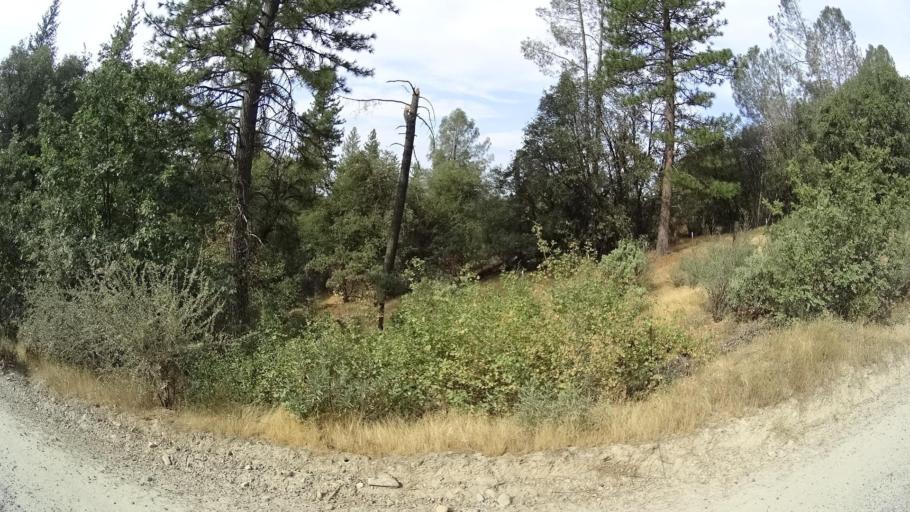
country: US
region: California
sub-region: Mariposa County
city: Midpines
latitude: 37.4963
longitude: -119.7958
